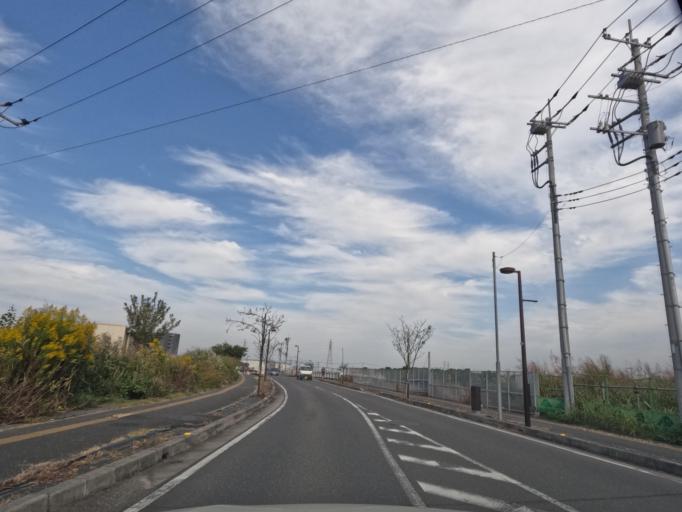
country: JP
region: Saitama
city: Koshigaya
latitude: 35.9020
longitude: 139.7255
